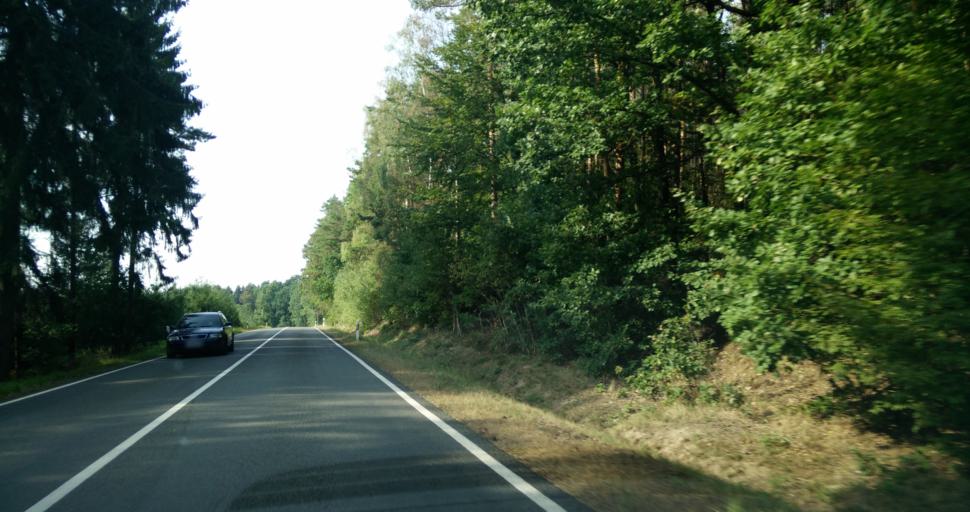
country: DE
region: Saxony
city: Grossbothen
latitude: 51.1361
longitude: 12.7510
